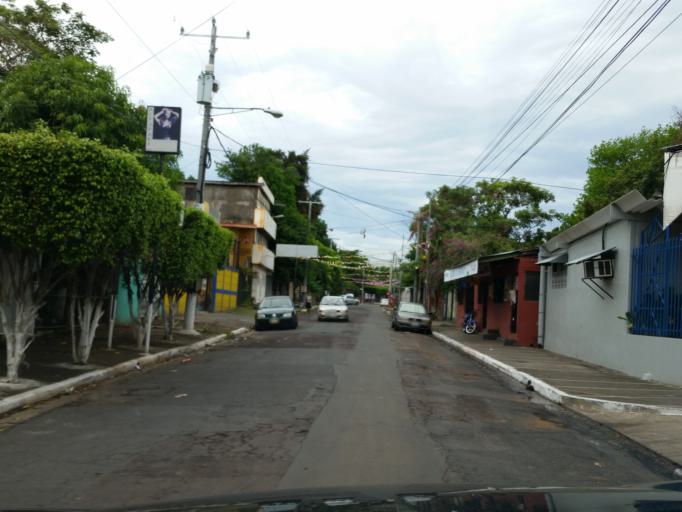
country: NI
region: Managua
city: Managua
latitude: 12.1459
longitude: -86.2833
